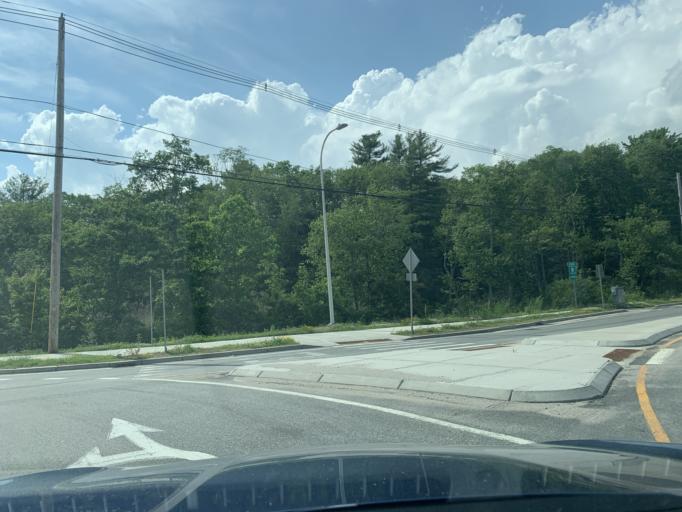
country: US
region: Rhode Island
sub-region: Kent County
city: Coventry
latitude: 41.6933
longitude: -71.6934
